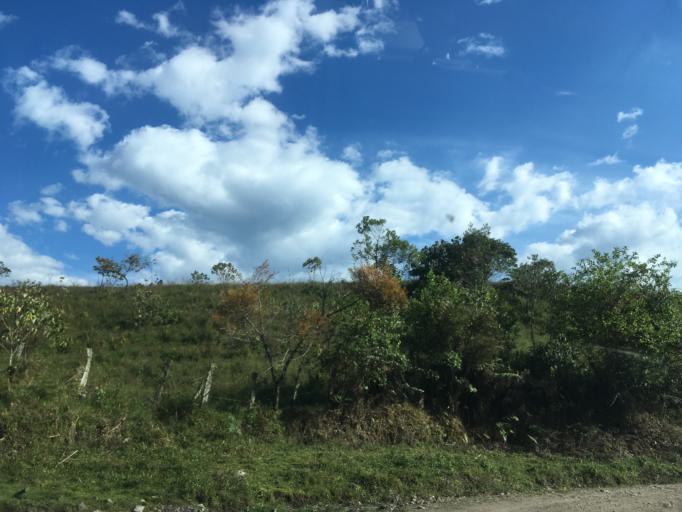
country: CO
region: Santander
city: Oiba
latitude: 6.1258
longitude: -73.1937
